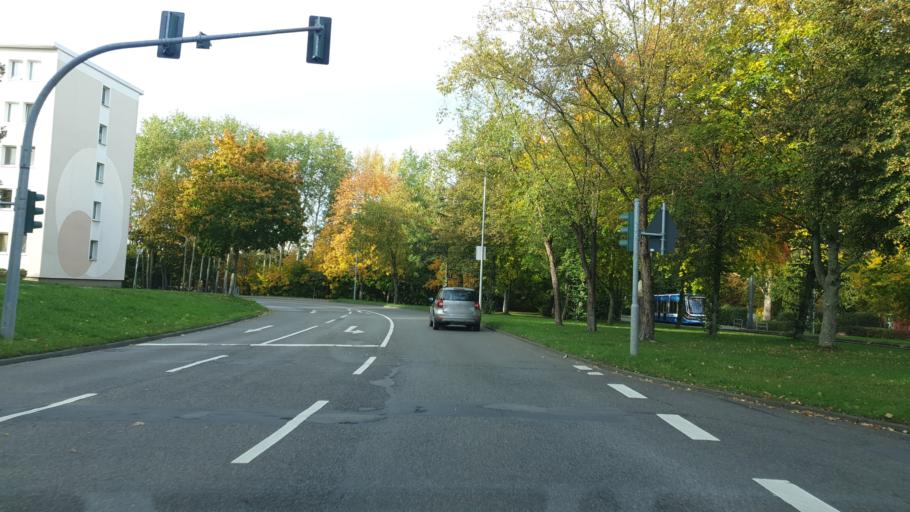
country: DE
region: Saxony
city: Hilbersdorf
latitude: 50.8217
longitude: 12.9636
